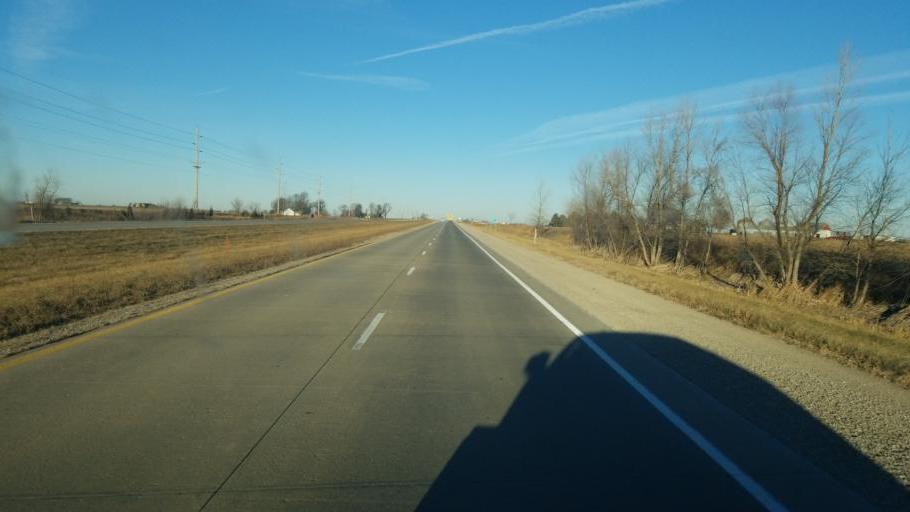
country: US
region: Iowa
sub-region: Mahaska County
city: Oskaloosa
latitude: 41.3552
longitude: -92.7637
